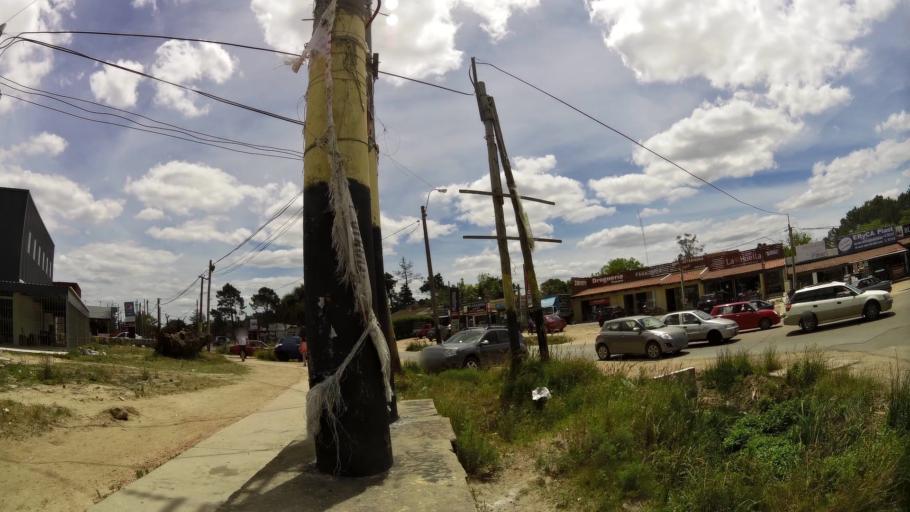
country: UY
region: Canelones
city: Pando
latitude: -34.8007
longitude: -55.9209
